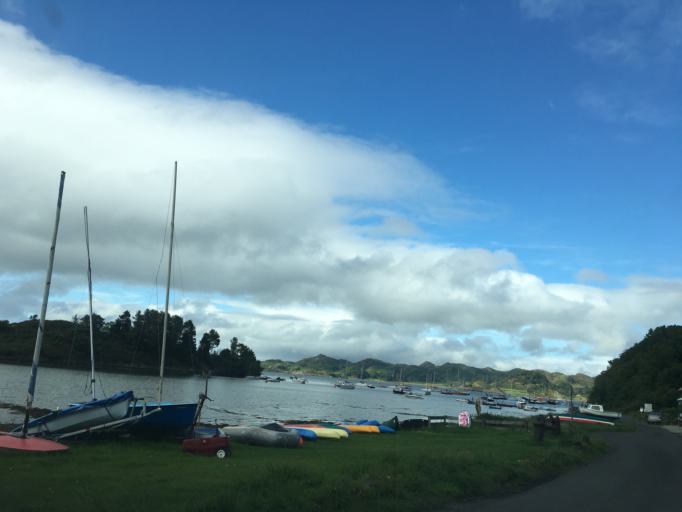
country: GB
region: Scotland
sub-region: Argyll and Bute
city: Ardrishaig
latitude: 56.0877
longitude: -5.5656
